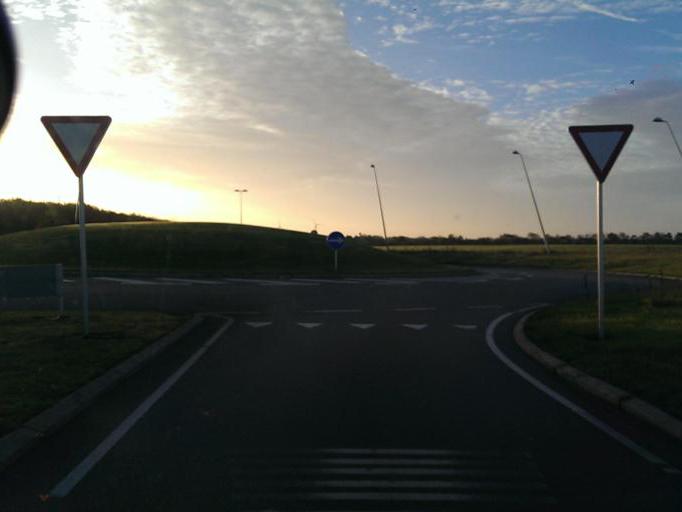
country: DK
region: South Denmark
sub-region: Esbjerg Kommune
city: Bramming
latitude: 55.4709
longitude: 8.6639
